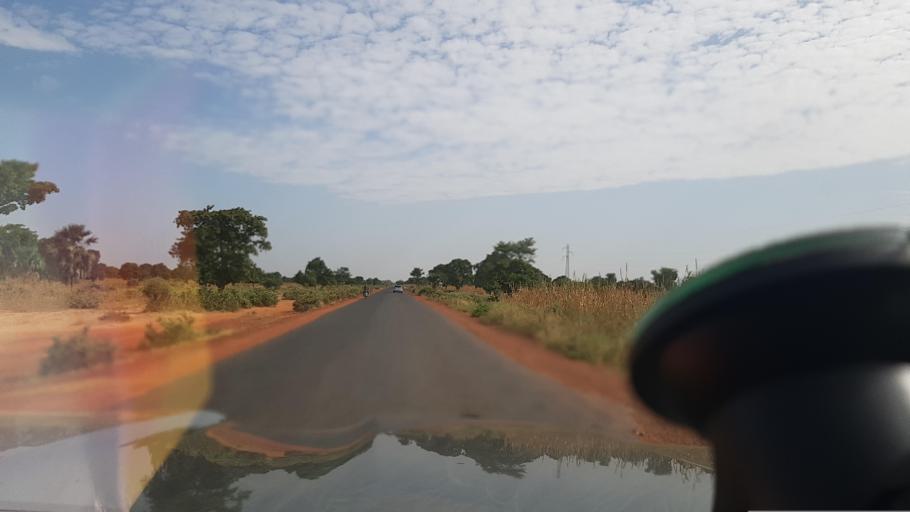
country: ML
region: Segou
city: Segou
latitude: 13.5097
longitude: -6.1437
